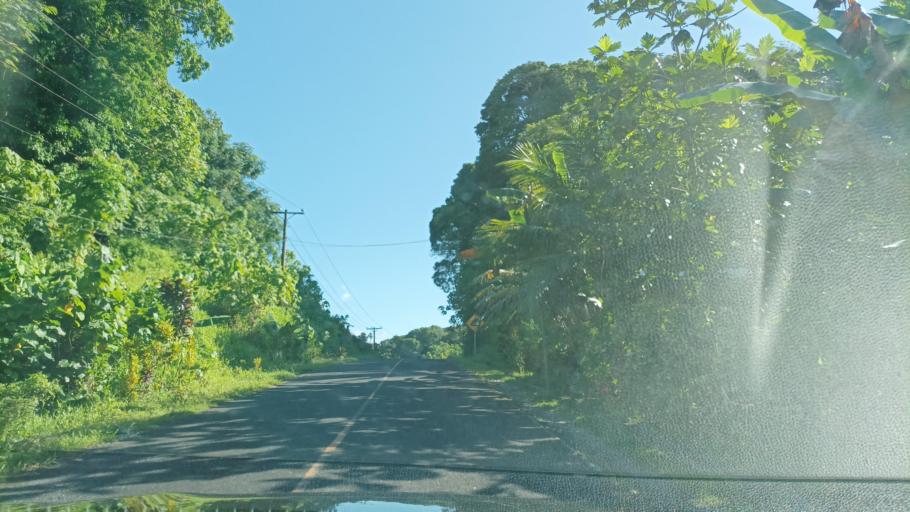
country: FM
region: Pohnpei
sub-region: Madolenihm Municipality
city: Madolenihm Municipality Government
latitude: 6.8134
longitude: 158.2941
